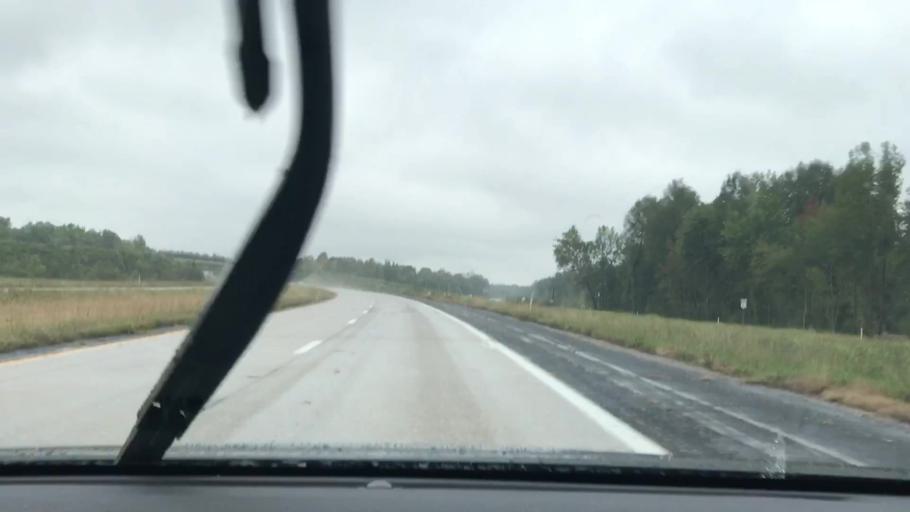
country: US
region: Kentucky
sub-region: Hopkins County
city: Nortonville
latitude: 37.1519
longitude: -87.4641
